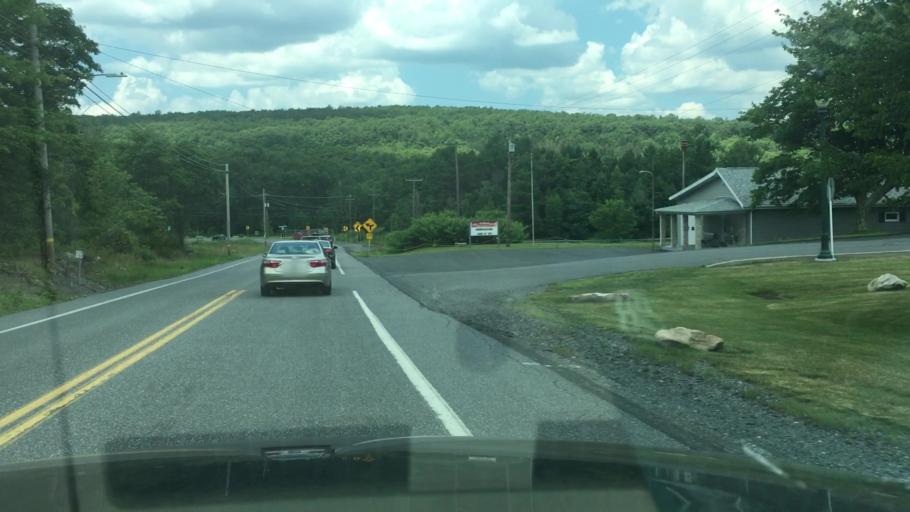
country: US
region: Pennsylvania
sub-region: Schuylkill County
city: Minersville
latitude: 40.7080
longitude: -76.3297
